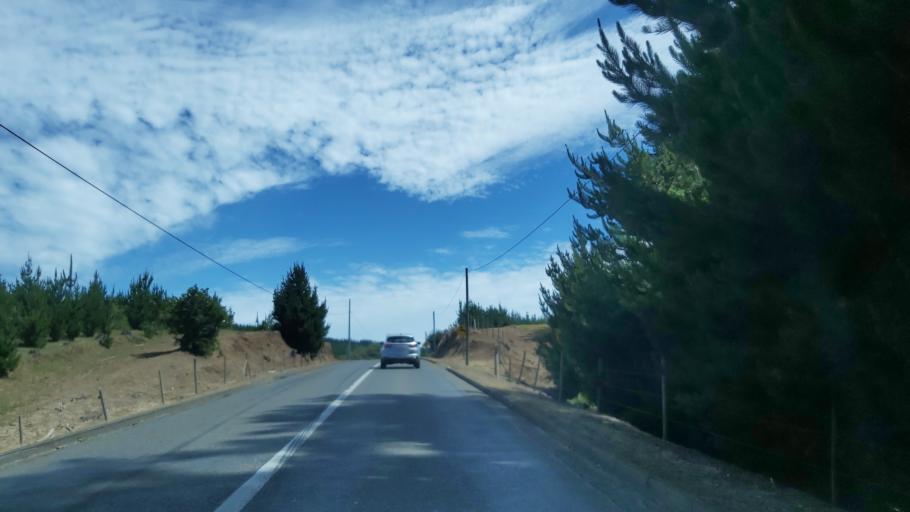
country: CL
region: Maule
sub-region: Provincia de Talca
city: Constitucion
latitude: -35.5160
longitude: -72.5298
